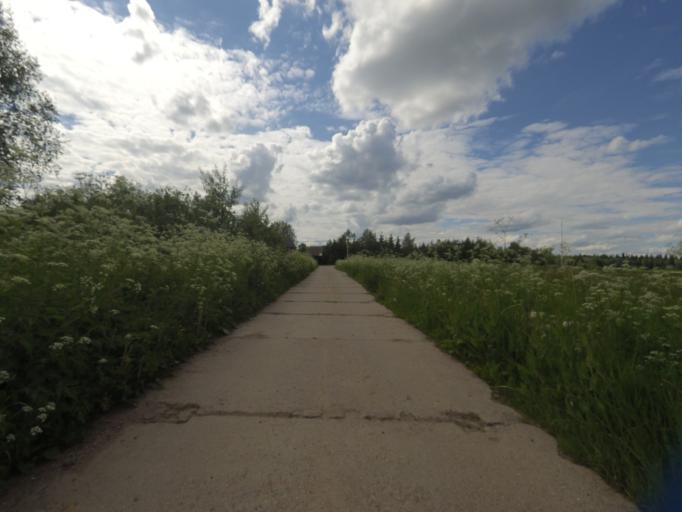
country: RU
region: Moskovskaya
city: Marfino
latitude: 56.0657
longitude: 37.6258
